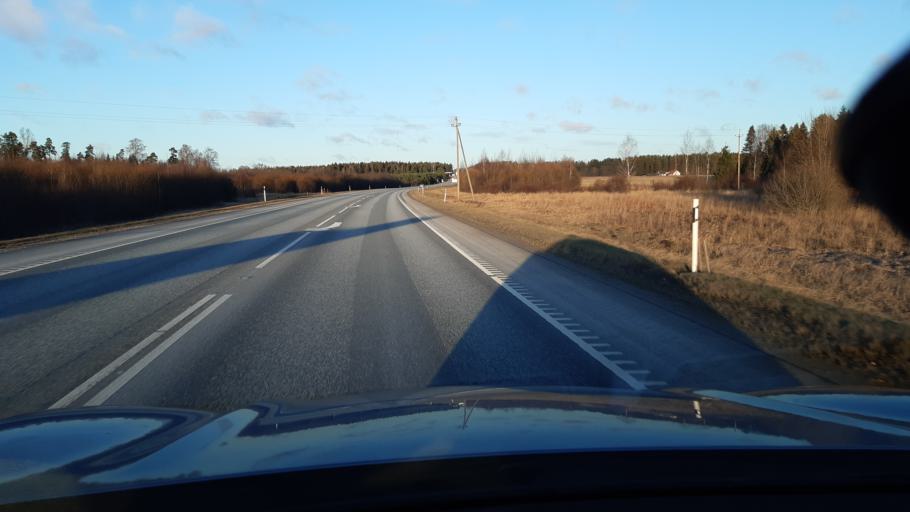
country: EE
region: Raplamaa
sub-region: Kohila vald
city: Kohila
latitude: 59.1741
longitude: 24.7743
